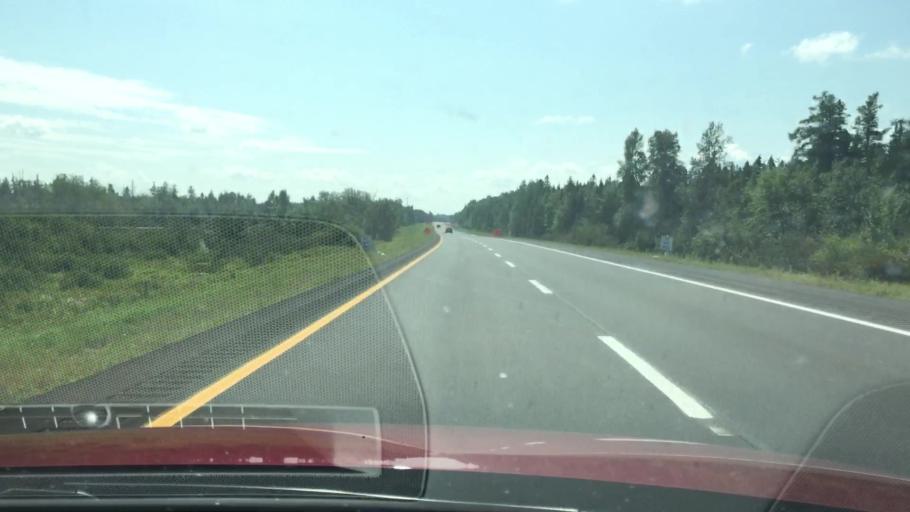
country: US
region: Maine
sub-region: Penobscot County
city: Patten
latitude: 45.8847
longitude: -68.4079
